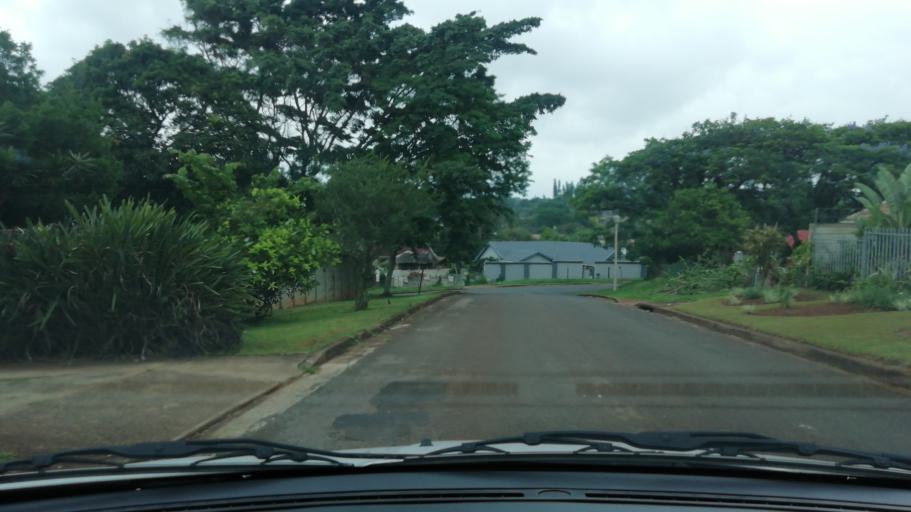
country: ZA
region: KwaZulu-Natal
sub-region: uThungulu District Municipality
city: Empangeni
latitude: -28.7602
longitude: 31.9011
